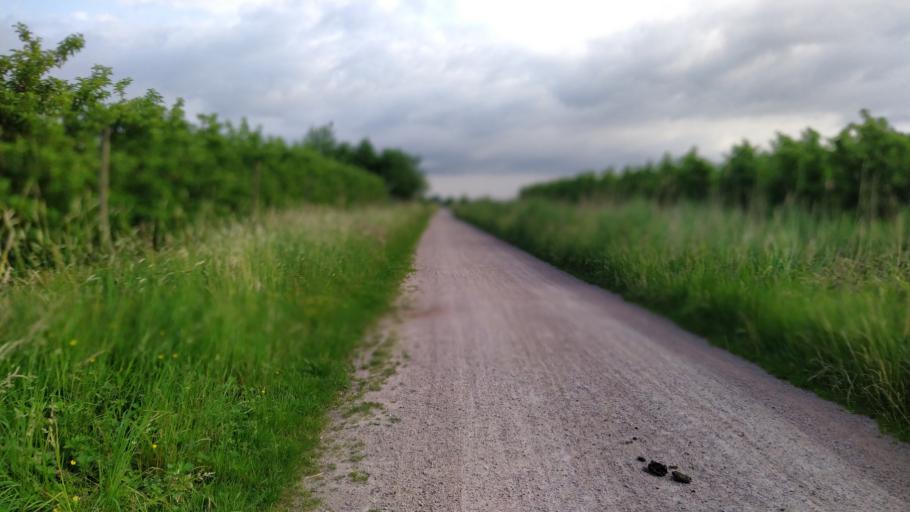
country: DE
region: Lower Saxony
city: Neu Wulmstorf
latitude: 53.5102
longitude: 9.8103
